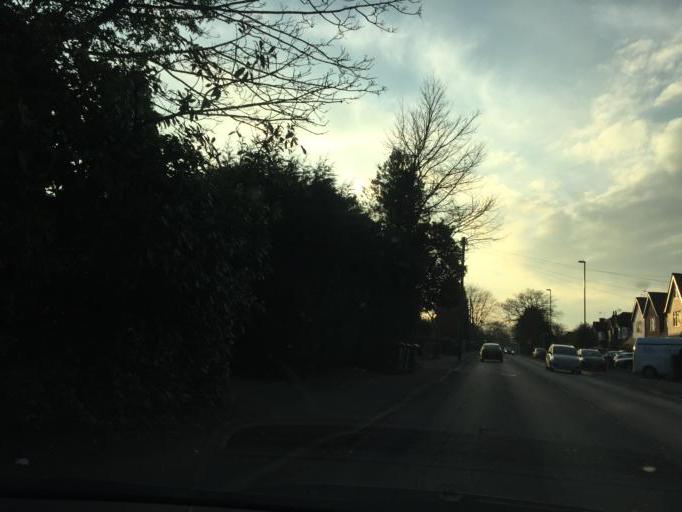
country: GB
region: England
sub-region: Coventry
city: Coventry
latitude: 52.4075
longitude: -1.5622
